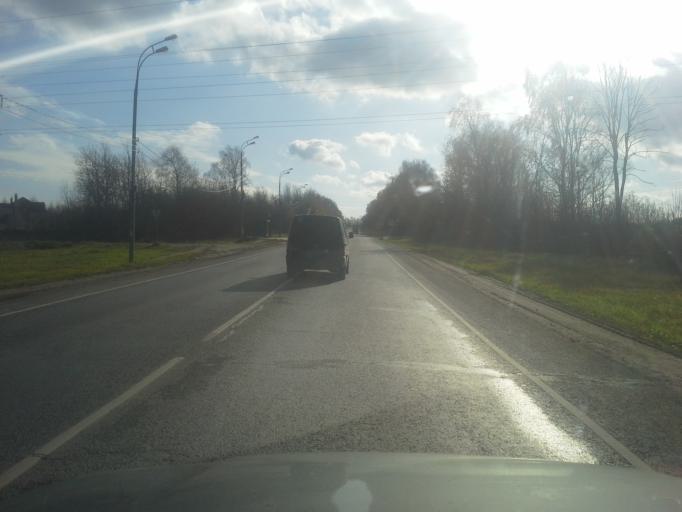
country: RU
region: Moskovskaya
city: Zvenigorod
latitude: 55.6895
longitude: 36.8962
